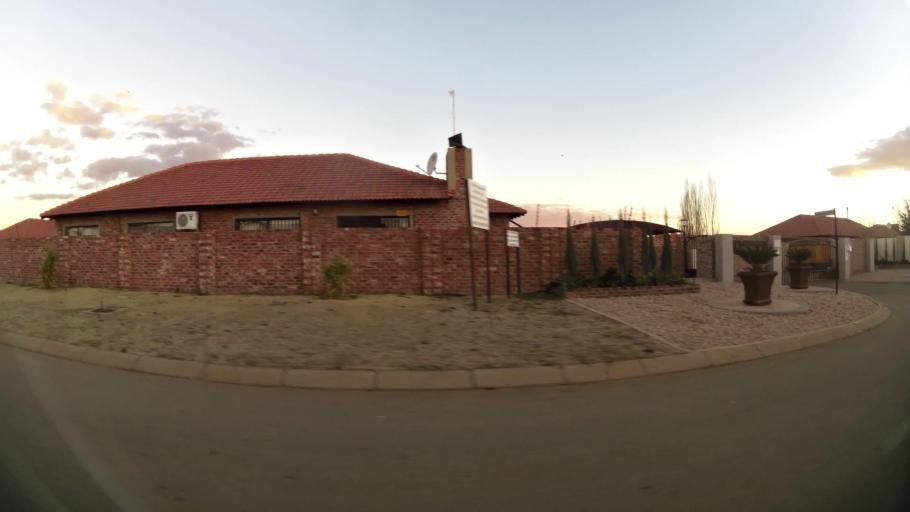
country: ZA
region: North-West
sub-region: Dr Kenneth Kaunda District Municipality
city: Potchefstroom
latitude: -26.7224
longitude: 27.1251
